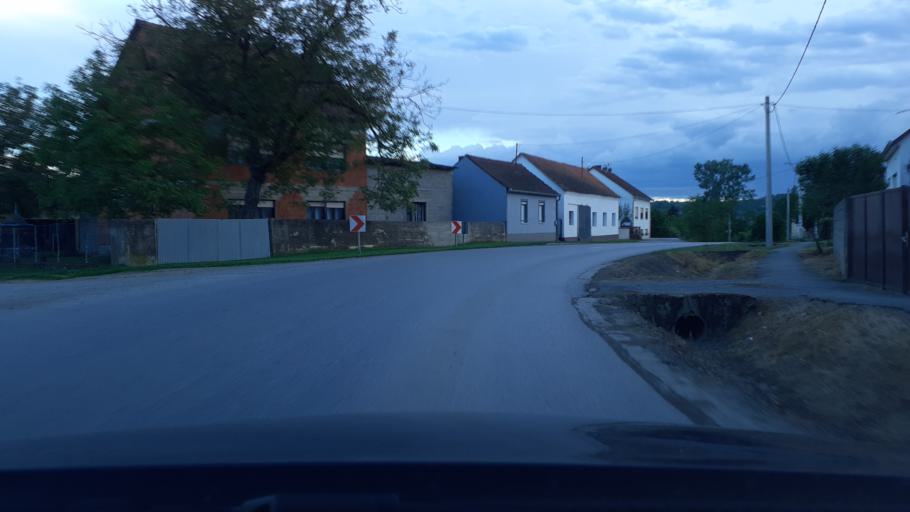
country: HR
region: Pozesko-Slavonska
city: Gradac
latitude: 45.3092
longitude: 17.8107
